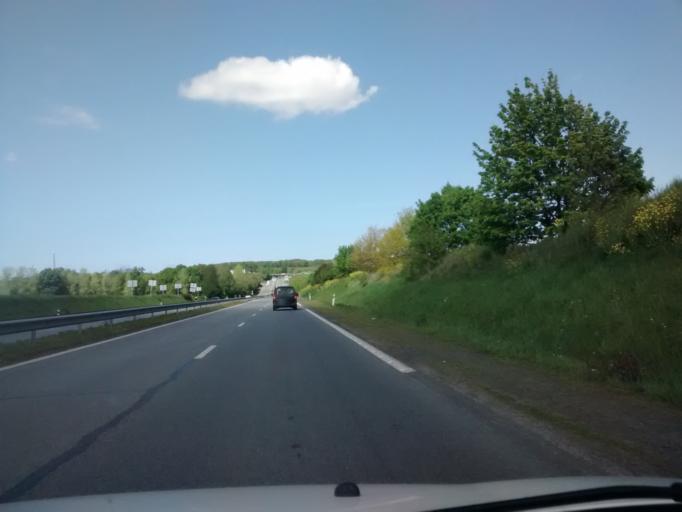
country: FR
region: Brittany
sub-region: Departement des Cotes-d'Armor
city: Saint-Samson-sur-Rance
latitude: 48.5122
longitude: -2.0391
